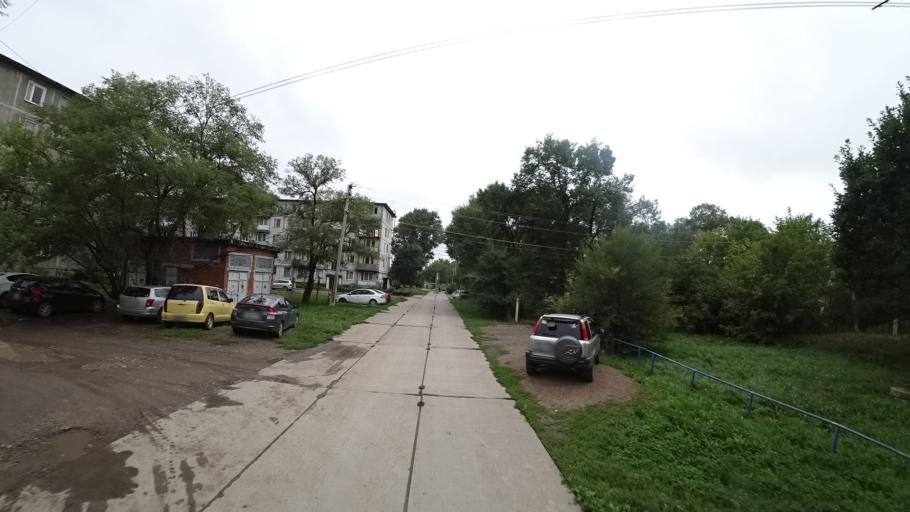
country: RU
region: Primorskiy
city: Chernigovka
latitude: 44.3331
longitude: 132.5377
